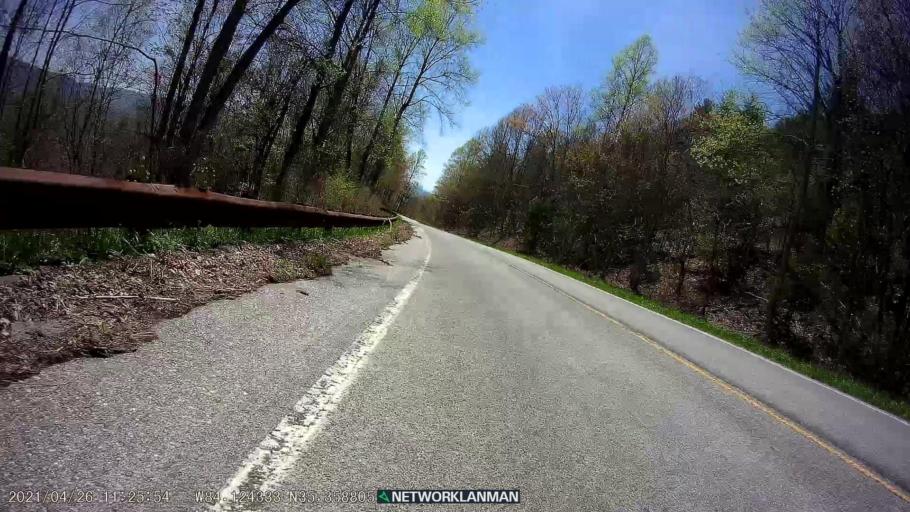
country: US
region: Tennessee
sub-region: Monroe County
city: Vonore
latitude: 35.3584
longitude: -84.1242
